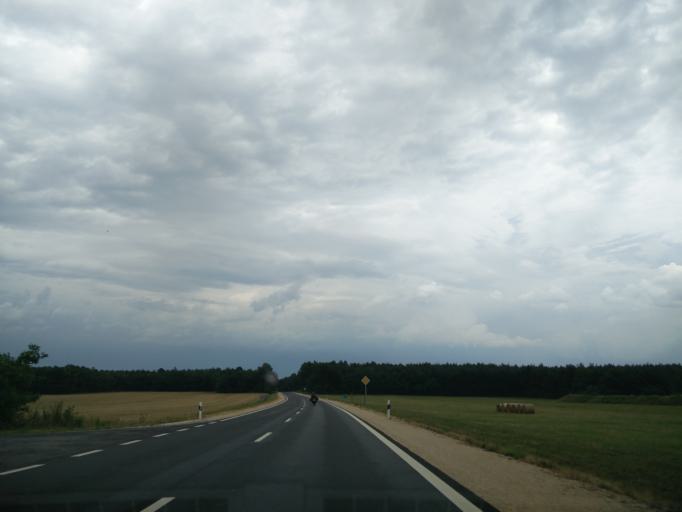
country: HU
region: Vas
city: Vasvar
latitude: 47.1027
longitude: 16.9329
